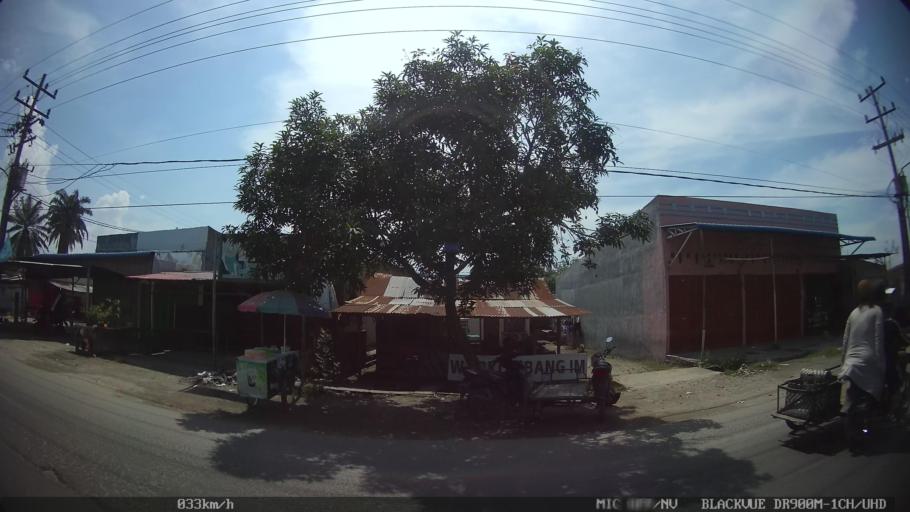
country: ID
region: North Sumatra
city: Medan
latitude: 3.6452
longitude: 98.6575
